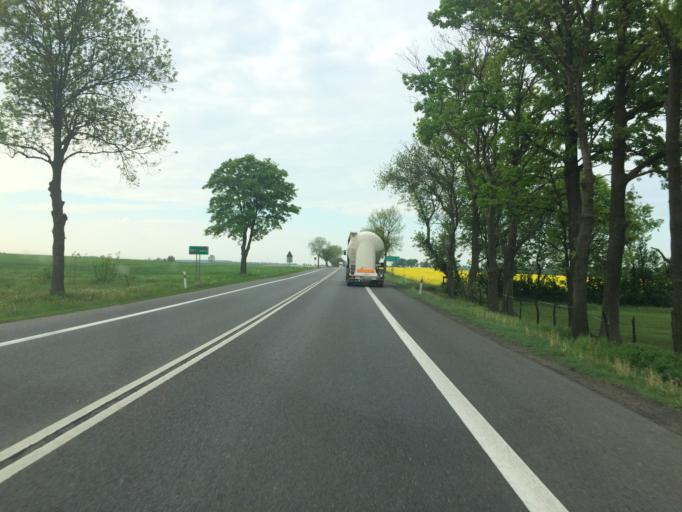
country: PL
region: Masovian Voivodeship
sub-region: Powiat mlawski
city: Wisniewo
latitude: 53.0585
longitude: 20.3463
